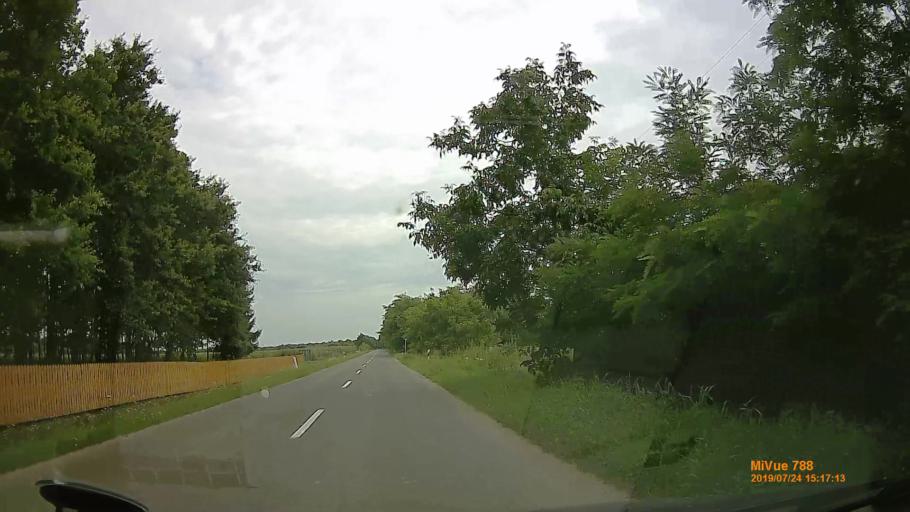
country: HU
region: Szabolcs-Szatmar-Bereg
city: Tarpa
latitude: 48.1948
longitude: 22.5473
